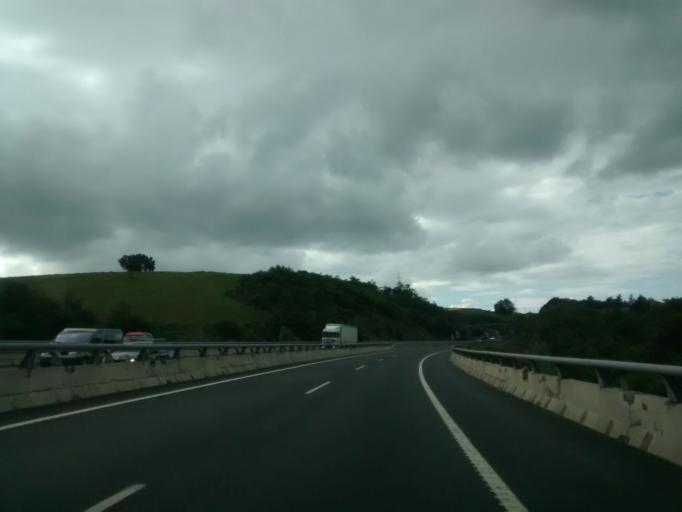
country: ES
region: Basque Country
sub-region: Provincia de Guipuzcoa
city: Lasarte
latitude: 43.2801
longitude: -2.0218
